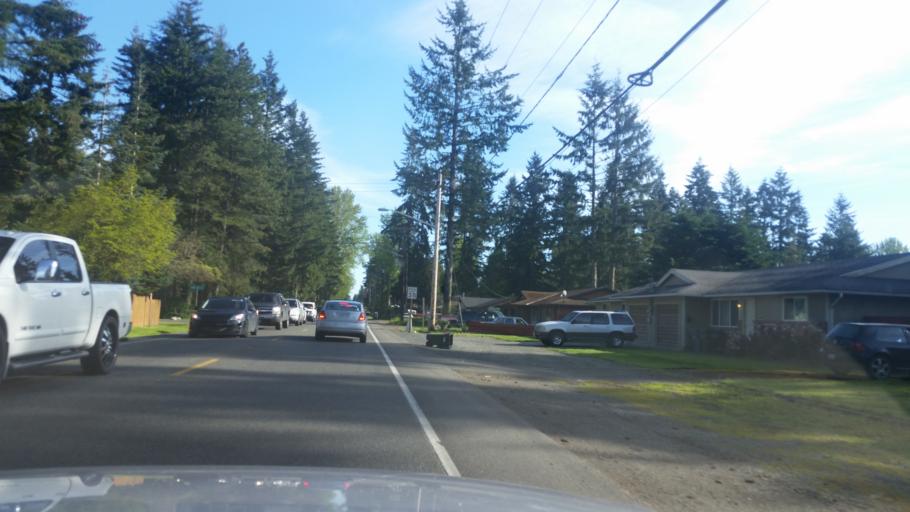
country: US
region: Washington
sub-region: Pierce County
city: South Hill
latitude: 47.1251
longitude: -122.2666
